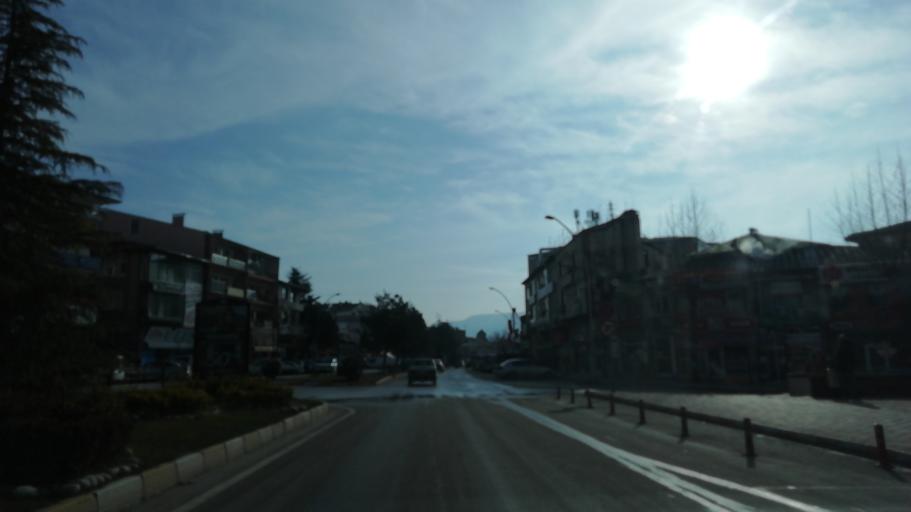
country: TR
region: Karabuk
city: Safranbolu
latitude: 41.2507
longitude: 32.6817
